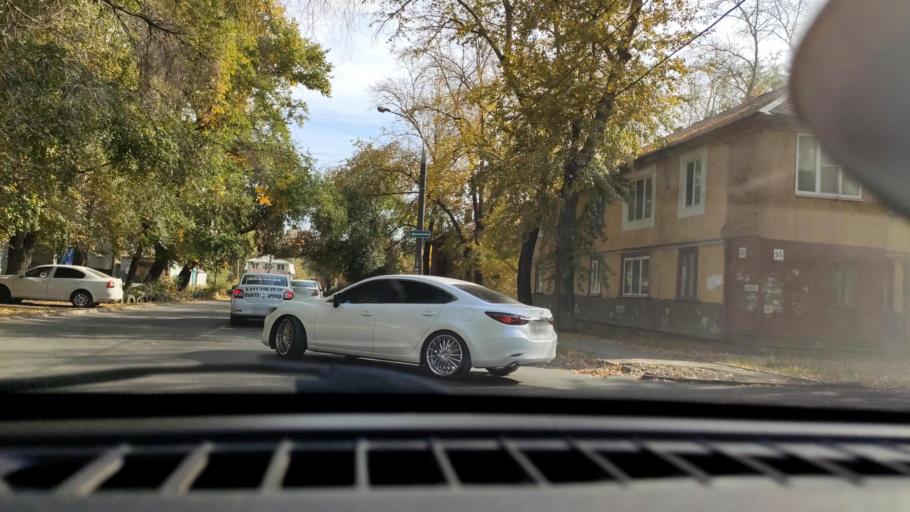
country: RU
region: Samara
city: Petra-Dubrava
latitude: 53.2345
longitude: 50.2837
